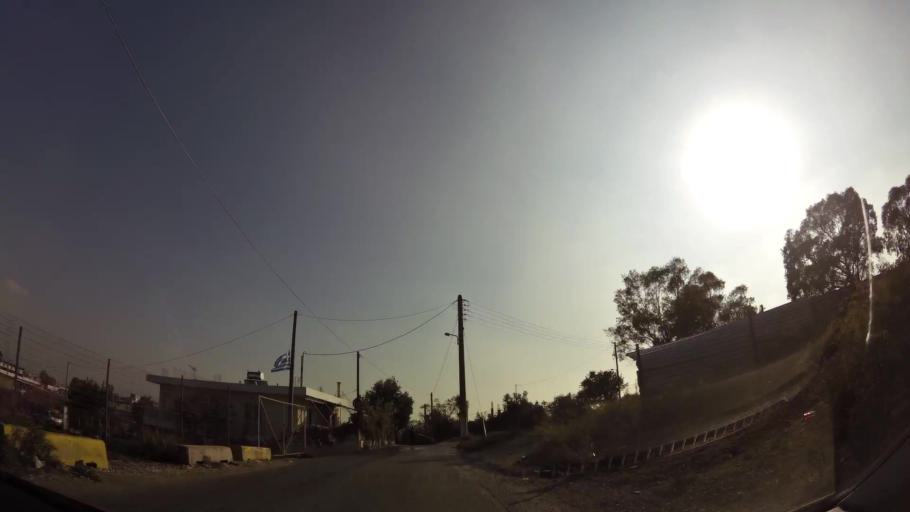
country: GR
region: Attica
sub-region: Nomarchia Anatolikis Attikis
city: Acharnes
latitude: 38.0697
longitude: 23.7323
